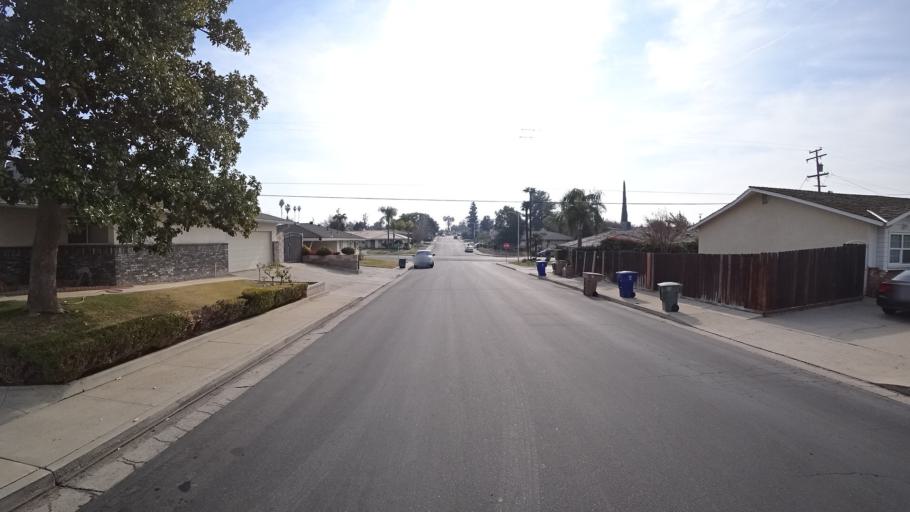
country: US
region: California
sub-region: Kern County
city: Oildale
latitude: 35.4092
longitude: -118.9627
